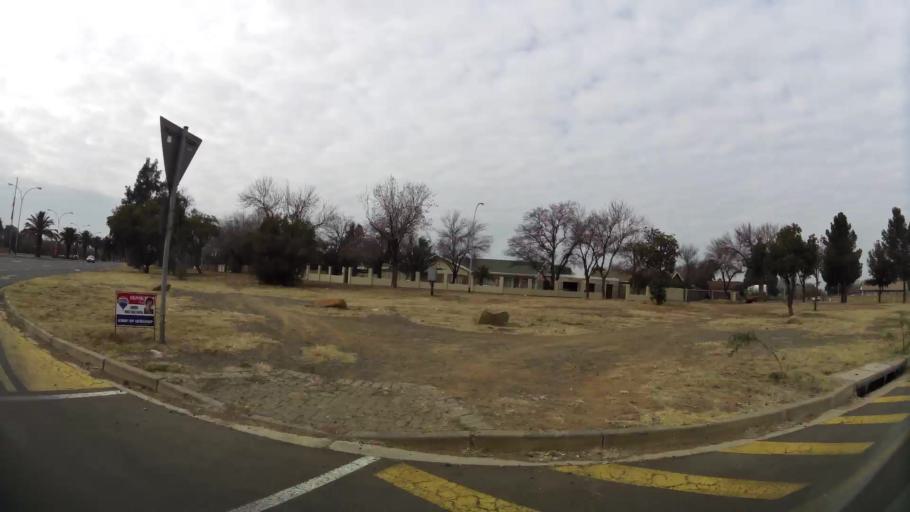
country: ZA
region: Orange Free State
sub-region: Mangaung Metropolitan Municipality
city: Bloemfontein
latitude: -29.1270
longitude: 26.1684
